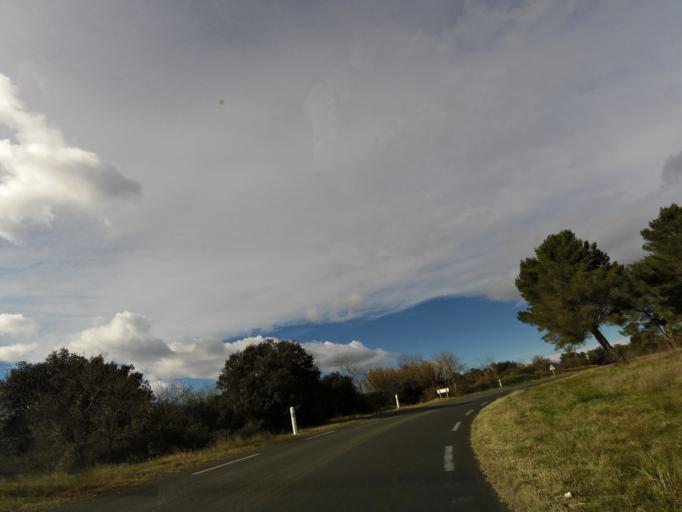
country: FR
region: Languedoc-Roussillon
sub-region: Departement du Gard
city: Aubais
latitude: 43.7545
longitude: 4.1132
